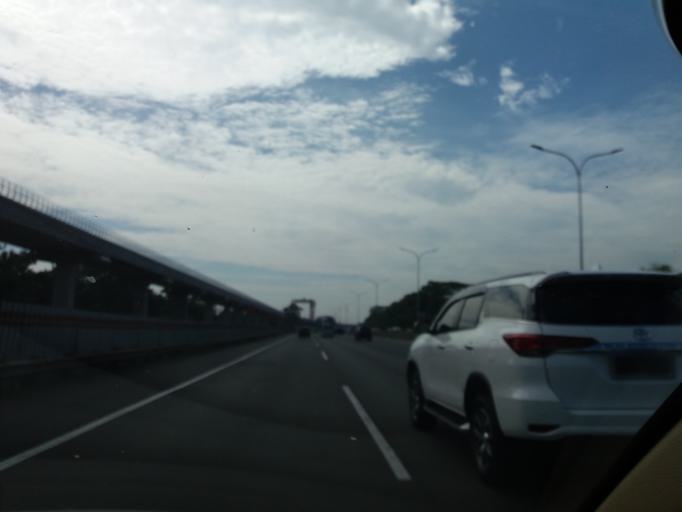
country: ID
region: West Java
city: Cileungsir
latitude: -6.3348
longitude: 106.8878
